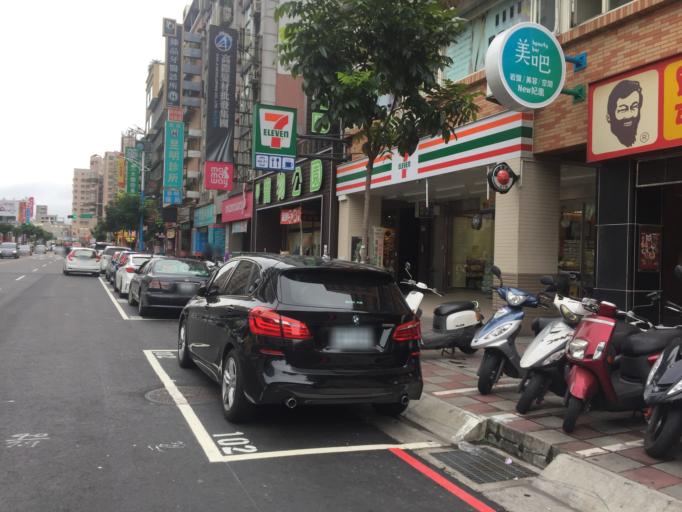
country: TW
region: Taipei
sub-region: Taipei
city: Banqiao
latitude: 25.0838
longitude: 121.4619
